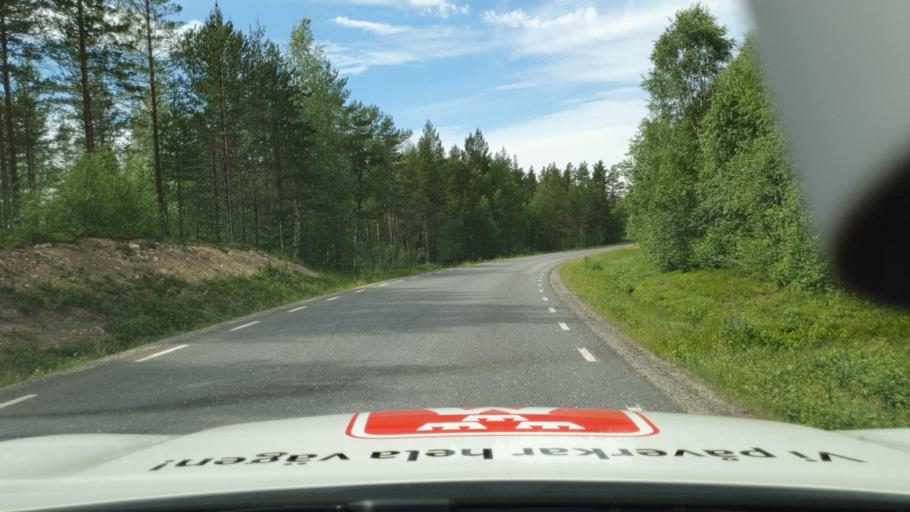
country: SE
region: Vaermland
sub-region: Torsby Kommun
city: Torsby
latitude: 60.6768
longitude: 12.6734
